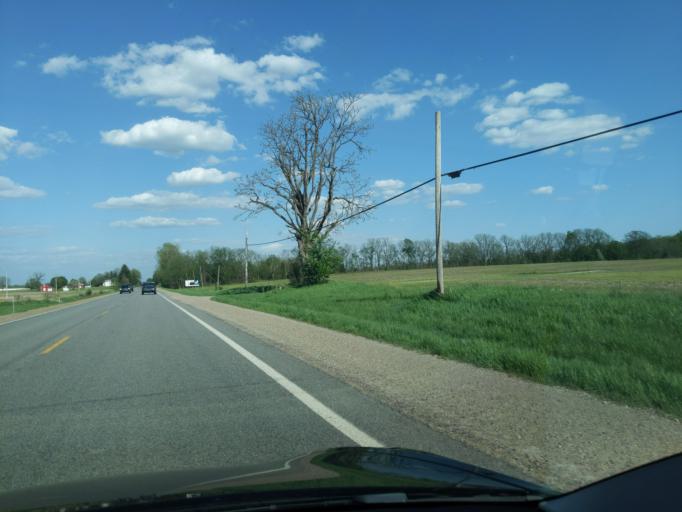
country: US
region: Michigan
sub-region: Eaton County
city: Grand Ledge
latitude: 42.7555
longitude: -84.7927
